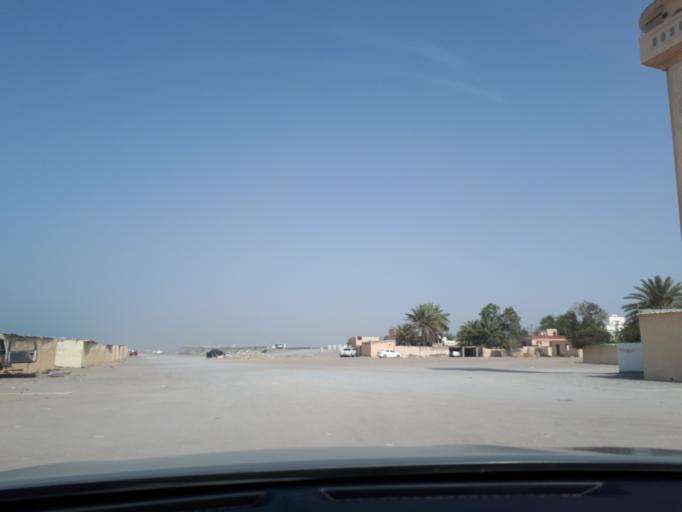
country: OM
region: Al Batinah
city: Barka'
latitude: 23.7076
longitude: 57.9347
